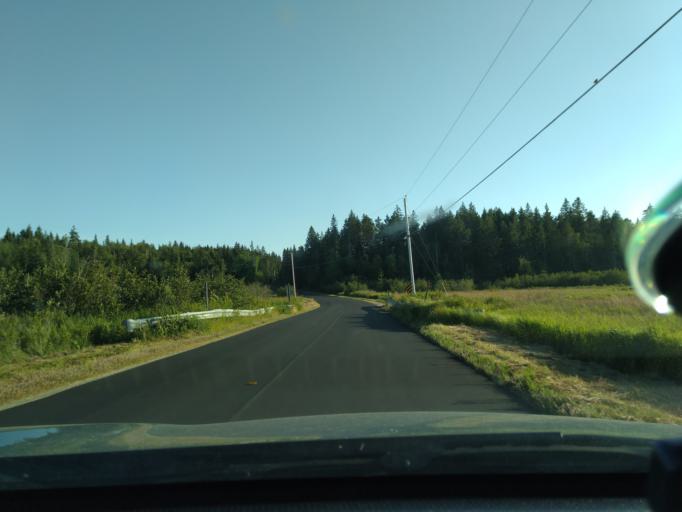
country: US
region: Maine
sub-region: Washington County
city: Machiasport
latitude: 44.6763
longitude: -67.1922
